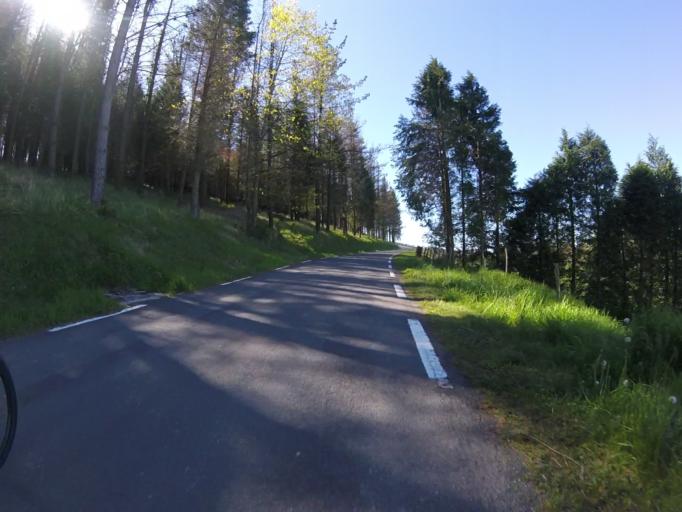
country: ES
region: Basque Country
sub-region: Provincia de Guipuzcoa
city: Errezil
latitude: 43.2103
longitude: -2.2011
